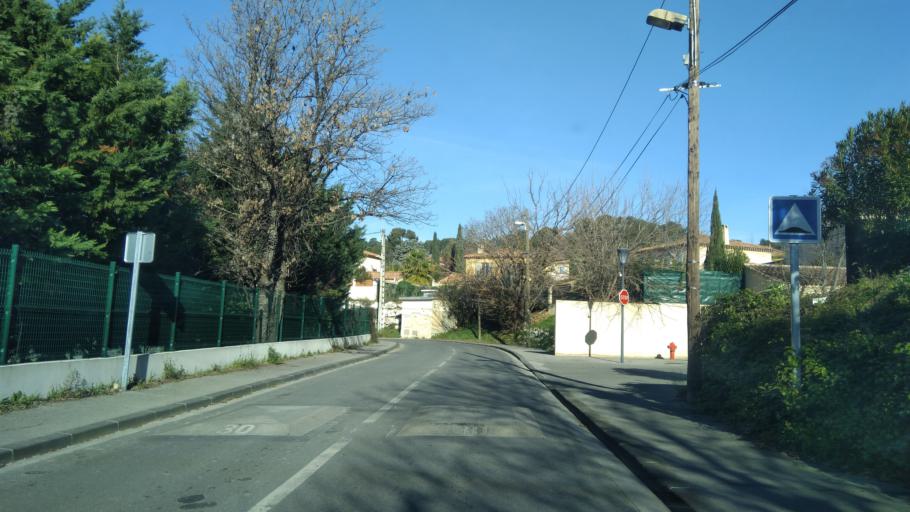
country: FR
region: Provence-Alpes-Cote d'Azur
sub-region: Departement des Bouches-du-Rhone
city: Marseille 12
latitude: 43.3024
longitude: 5.4572
